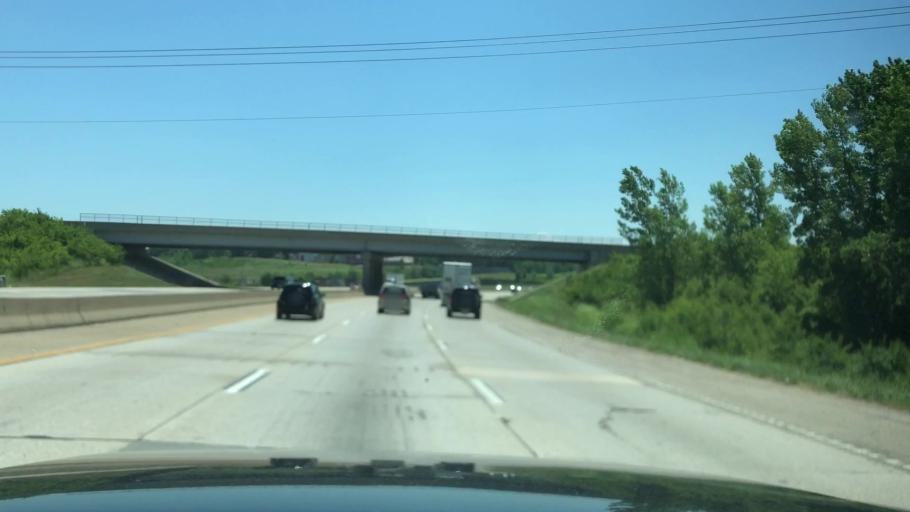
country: US
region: Missouri
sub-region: Saint Louis County
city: Bridgeton
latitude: 38.7877
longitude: -90.4216
